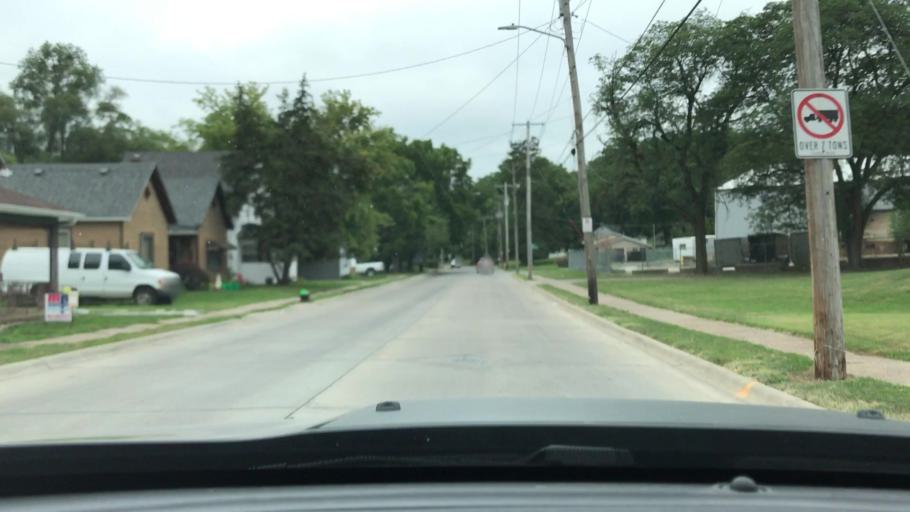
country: US
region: Illinois
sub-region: Rock Island County
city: Rock Island
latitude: 41.5170
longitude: -90.6226
